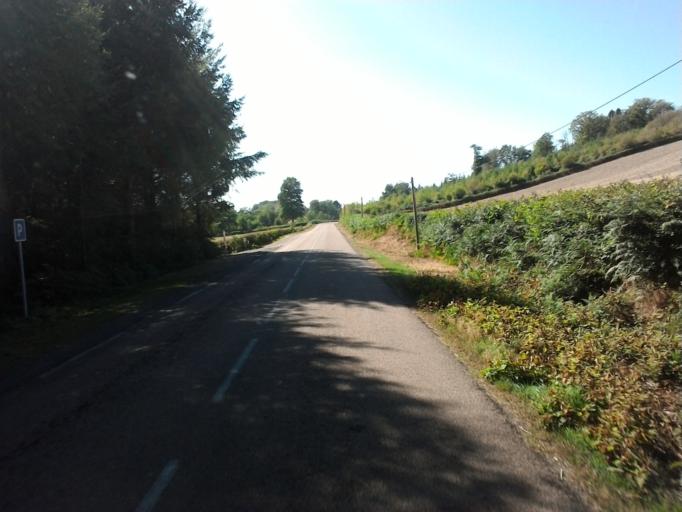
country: FR
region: Bourgogne
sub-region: Departement de la Nievre
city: Lormes
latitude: 47.2741
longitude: 3.9831
